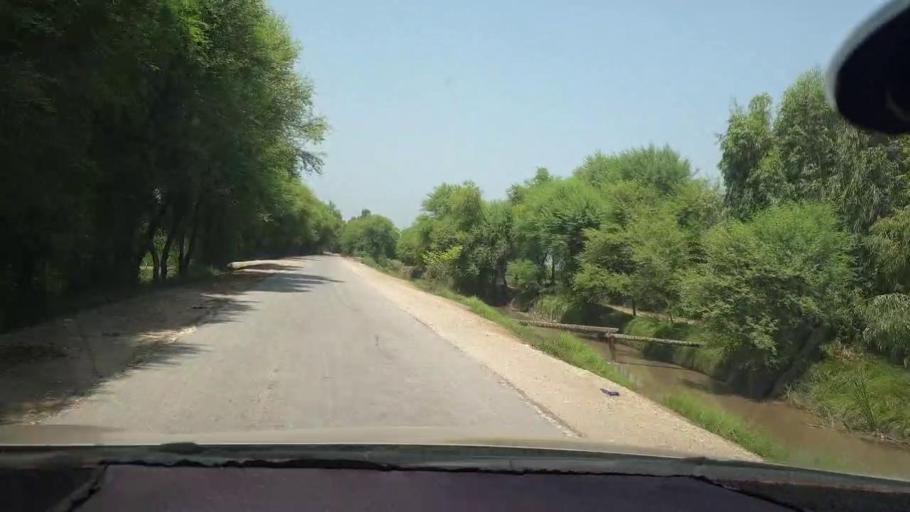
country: PK
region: Sindh
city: Kambar
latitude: 27.6546
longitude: 67.9622
